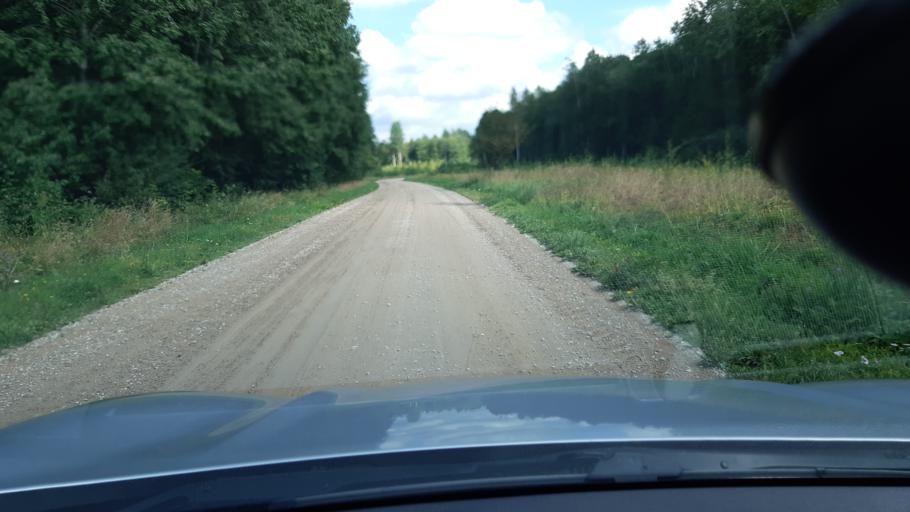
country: EE
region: Jaervamaa
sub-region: Tueri vald
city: Tueri
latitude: 58.9237
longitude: 25.2048
